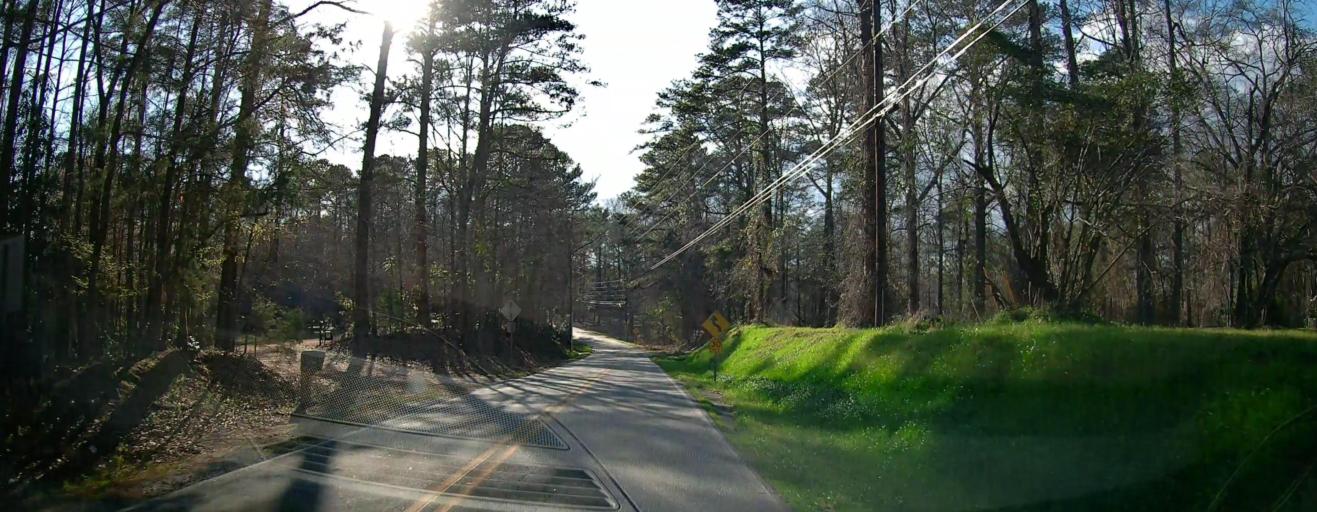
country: US
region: Georgia
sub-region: Harris County
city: Hamilton
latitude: 32.5761
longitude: -84.8147
